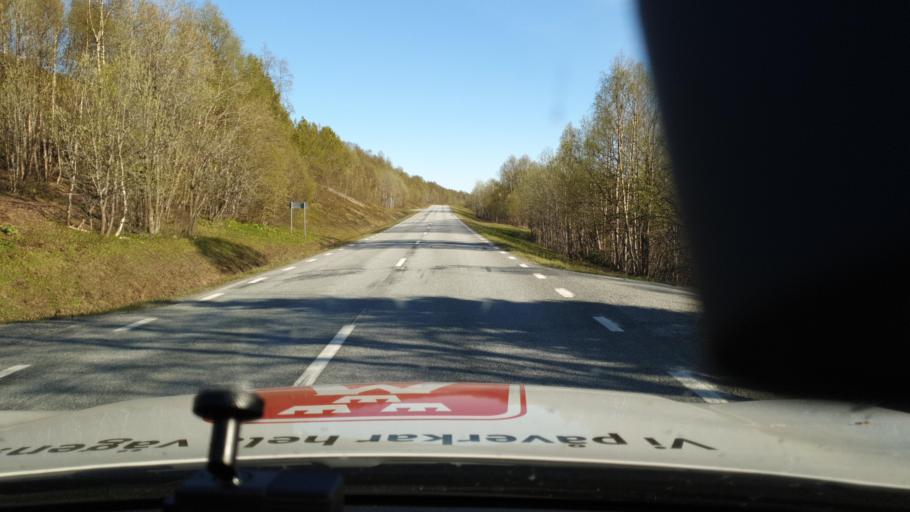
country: NO
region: Nordland
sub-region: Rana
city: Mo i Rana
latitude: 65.8604
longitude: 15.0252
